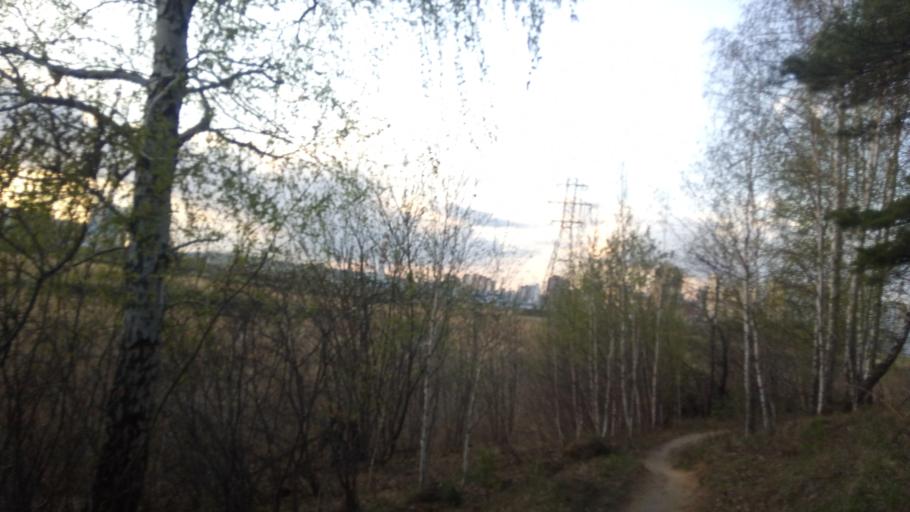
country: RU
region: Chelyabinsk
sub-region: Gorod Chelyabinsk
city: Chelyabinsk
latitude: 55.1624
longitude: 61.3126
